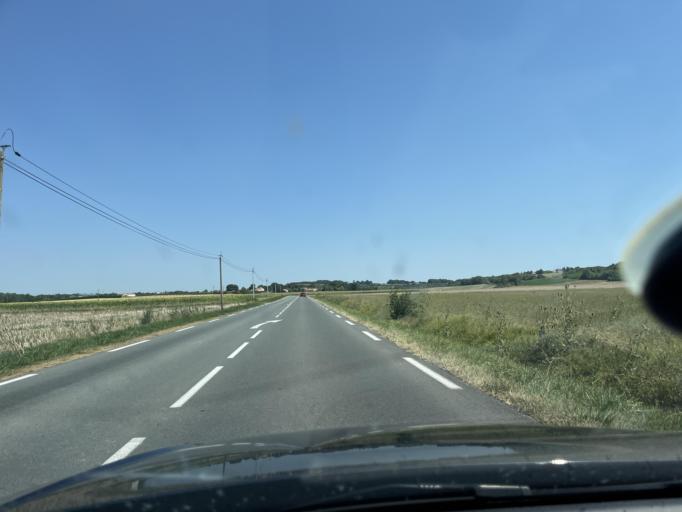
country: FR
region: Poitou-Charentes
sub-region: Departement de la Charente-Maritime
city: Mirambeau
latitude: 45.4175
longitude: -0.6263
